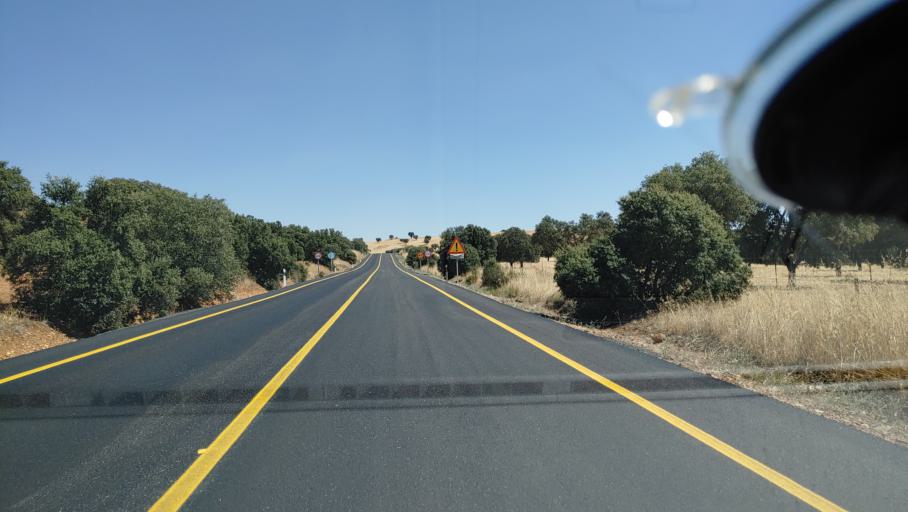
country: ES
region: Castille-La Mancha
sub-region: Provincia de Ciudad Real
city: Saceruela
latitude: 39.0151
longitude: -4.4689
